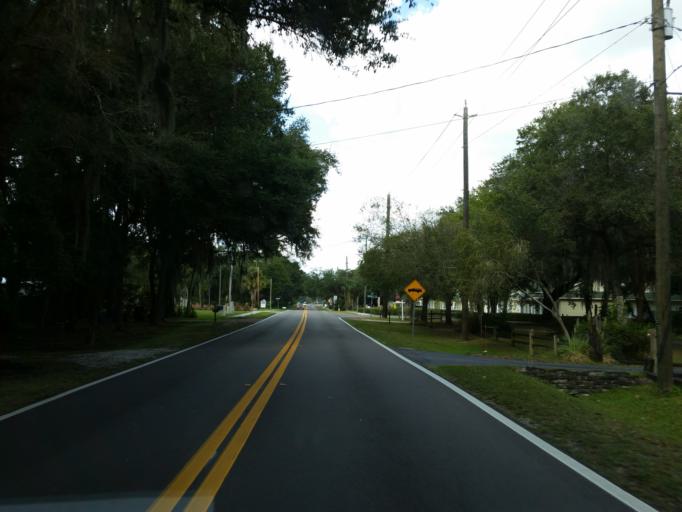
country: US
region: Florida
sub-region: Hillsborough County
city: Riverview
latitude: 27.8619
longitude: -82.3220
